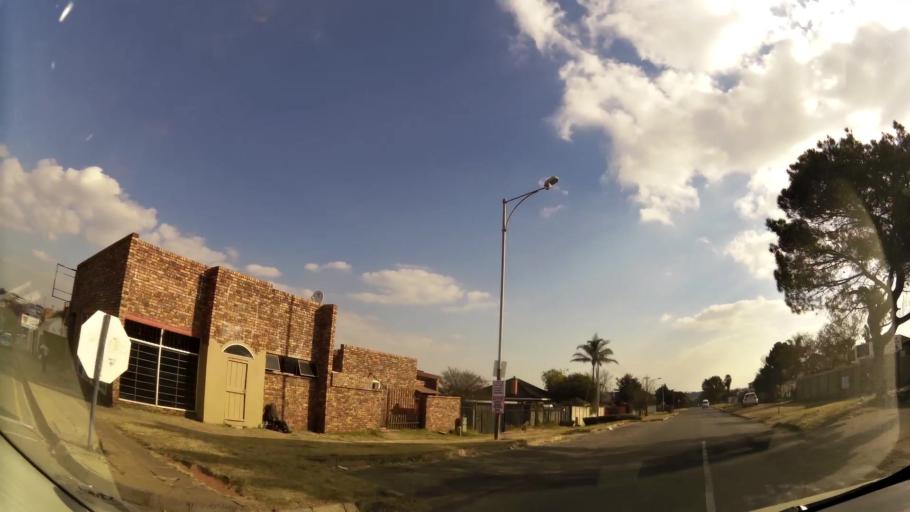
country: ZA
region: Gauteng
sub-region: West Rand District Municipality
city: Krugersdorp
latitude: -26.0928
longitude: 27.7687
